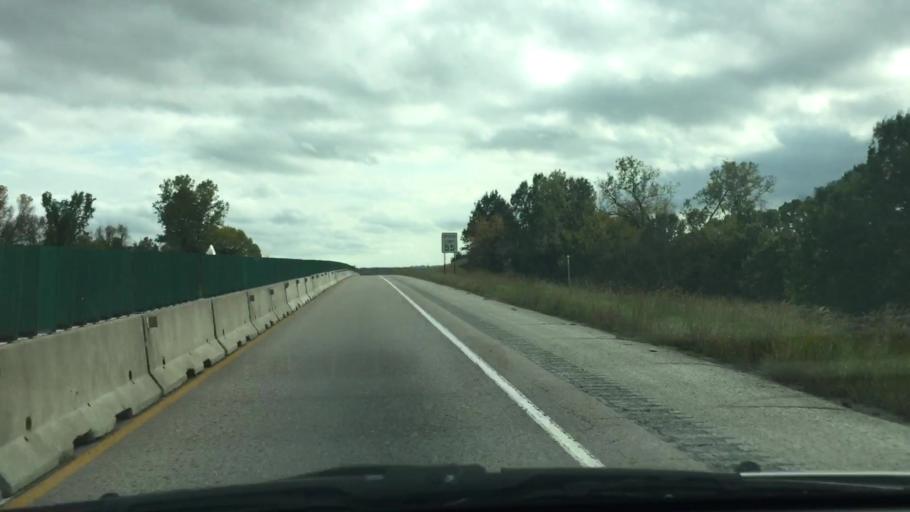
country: US
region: Iowa
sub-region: Decatur County
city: Leon
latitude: 40.6914
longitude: -93.8462
